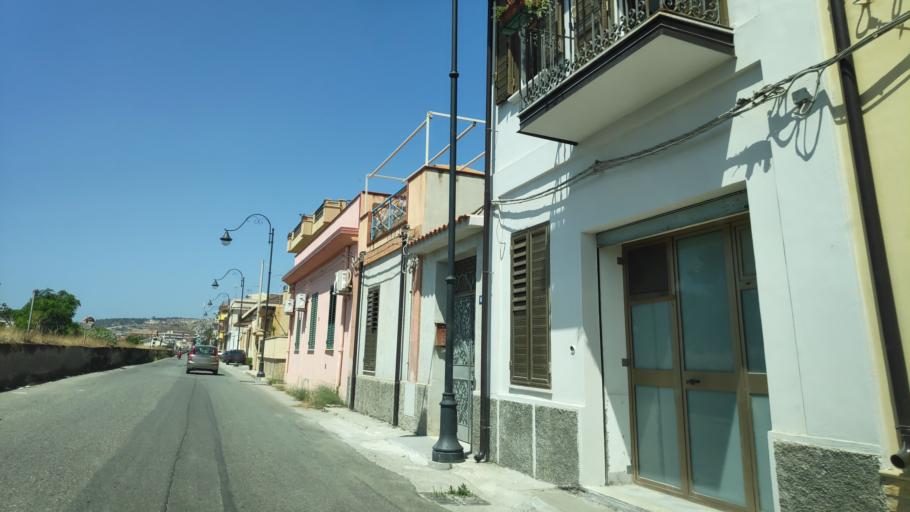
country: IT
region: Calabria
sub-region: Provincia di Reggio Calabria
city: Bova Marina
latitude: 37.9295
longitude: 15.9294
